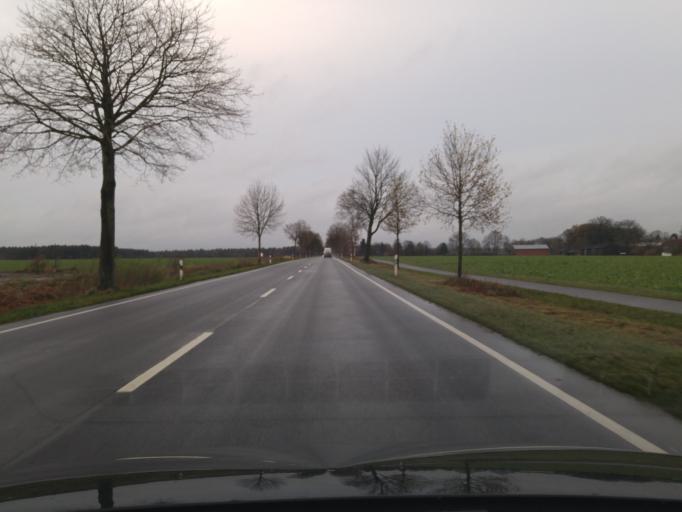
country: DE
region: Lower Saxony
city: Gross Oesingen
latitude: 52.6616
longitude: 10.4658
